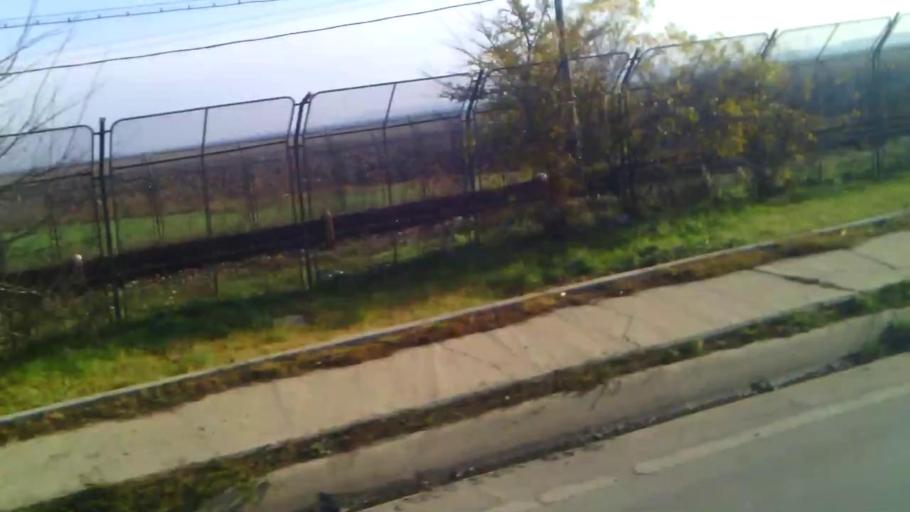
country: RO
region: Ilfov
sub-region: Comuna Popesti-Leordeni
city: Popesti-Leordeni
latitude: 44.3497
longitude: 26.1580
